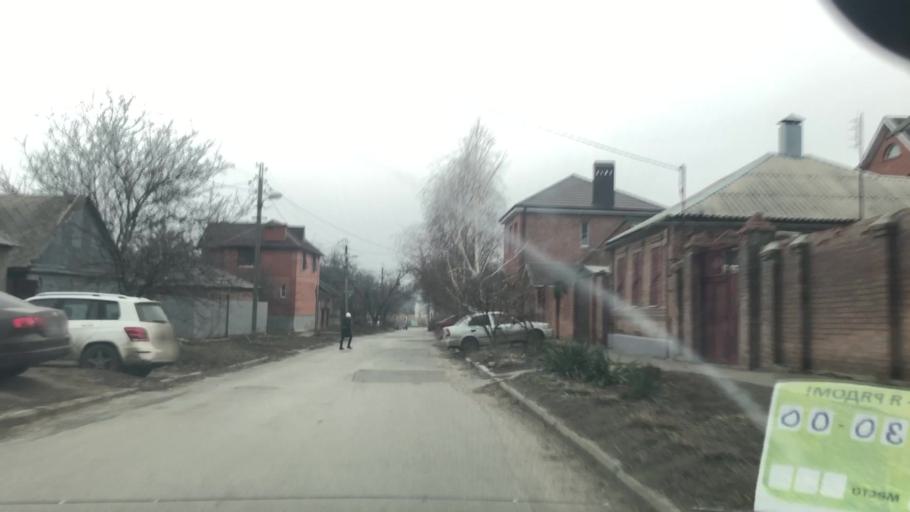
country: RU
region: Rostov
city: Rostov-na-Donu
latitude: 47.2323
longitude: 39.6817
